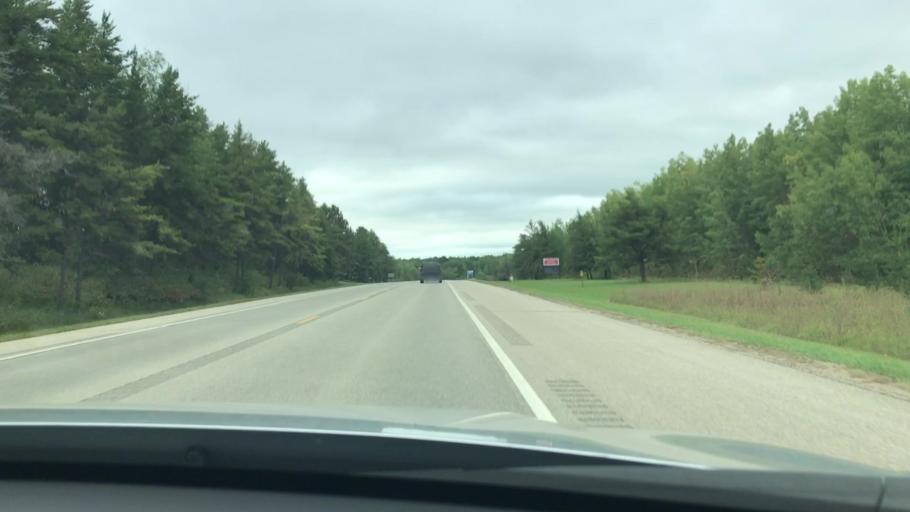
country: US
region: Minnesota
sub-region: Wadena County
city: Menahga
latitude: 46.8378
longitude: -95.0861
